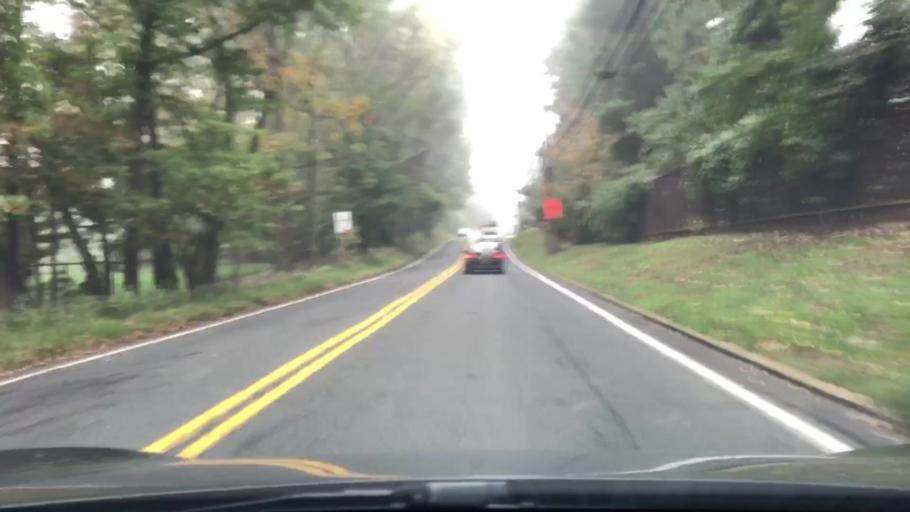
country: US
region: Pennsylvania
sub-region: Delaware County
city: Radnor
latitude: 40.0211
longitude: -75.3688
